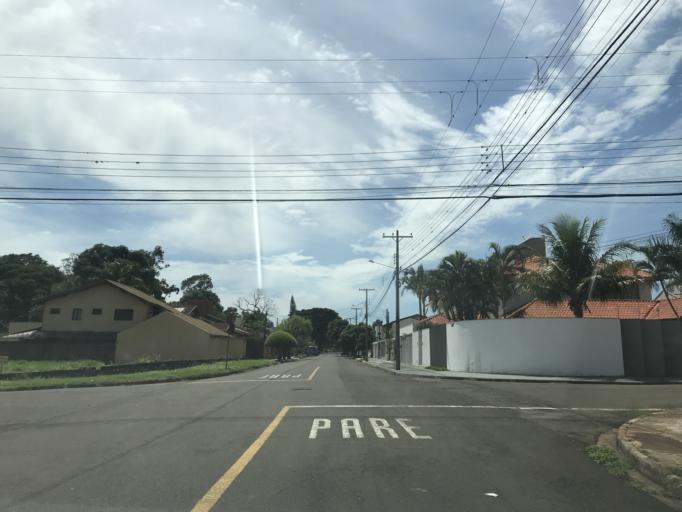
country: BR
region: Parana
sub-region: Londrina
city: Londrina
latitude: -23.3432
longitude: -51.1568
